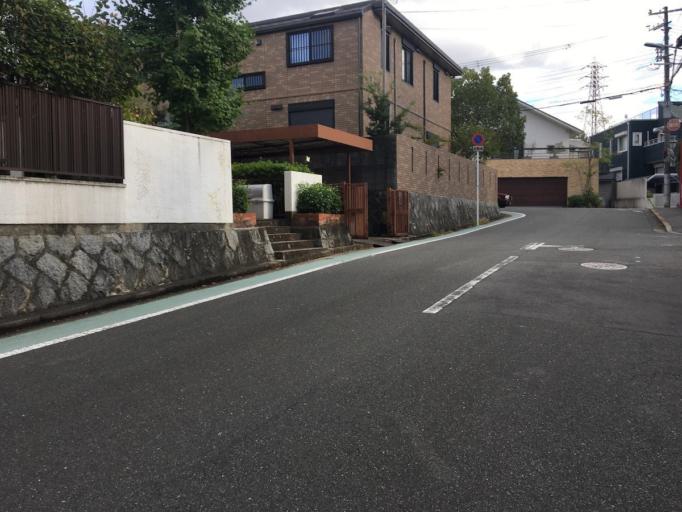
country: JP
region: Osaka
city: Suita
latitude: 34.8002
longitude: 135.5168
